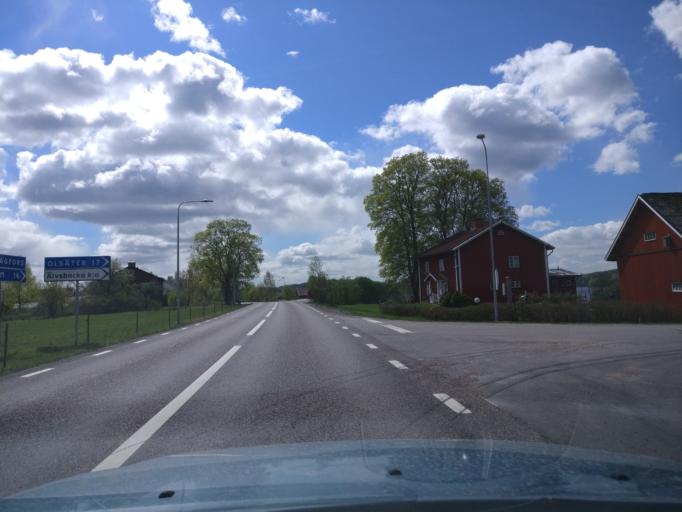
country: SE
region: Vaermland
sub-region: Karlstads Kommun
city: Molkom
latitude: 59.7175
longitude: 13.6756
